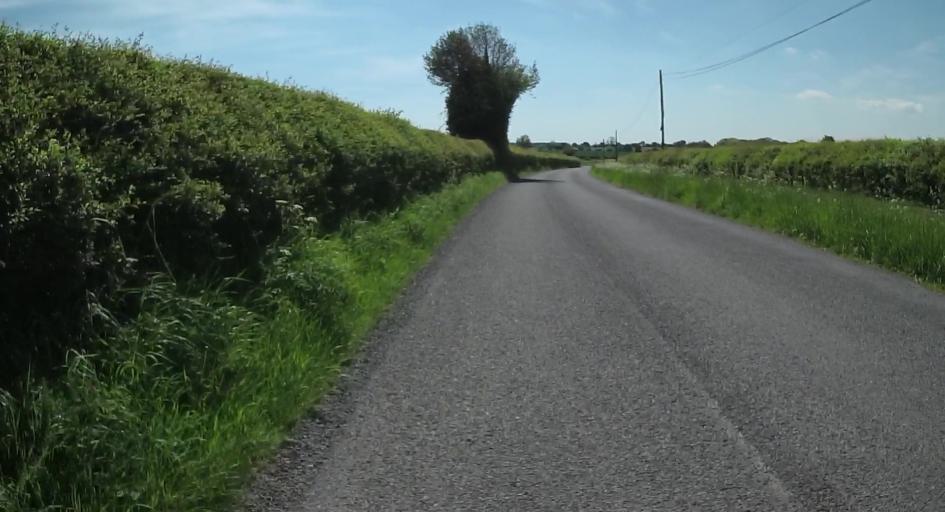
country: GB
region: England
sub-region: Hampshire
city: Four Marks
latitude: 51.1560
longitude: -1.1381
